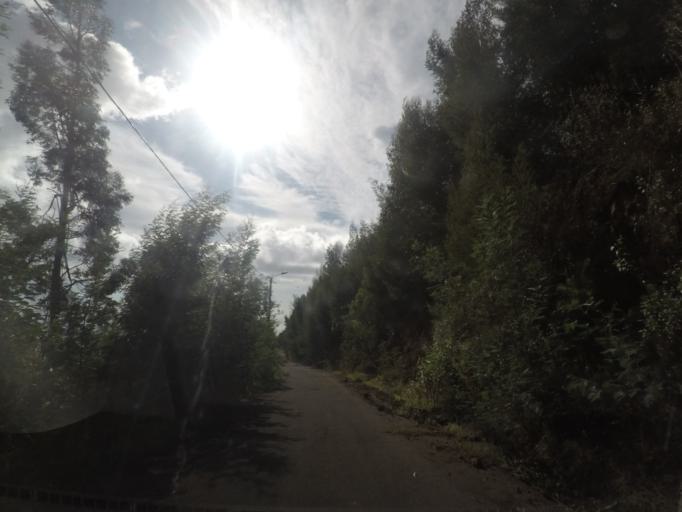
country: PT
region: Madeira
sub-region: Funchal
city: Nossa Senhora do Monte
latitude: 32.6798
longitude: -16.8900
